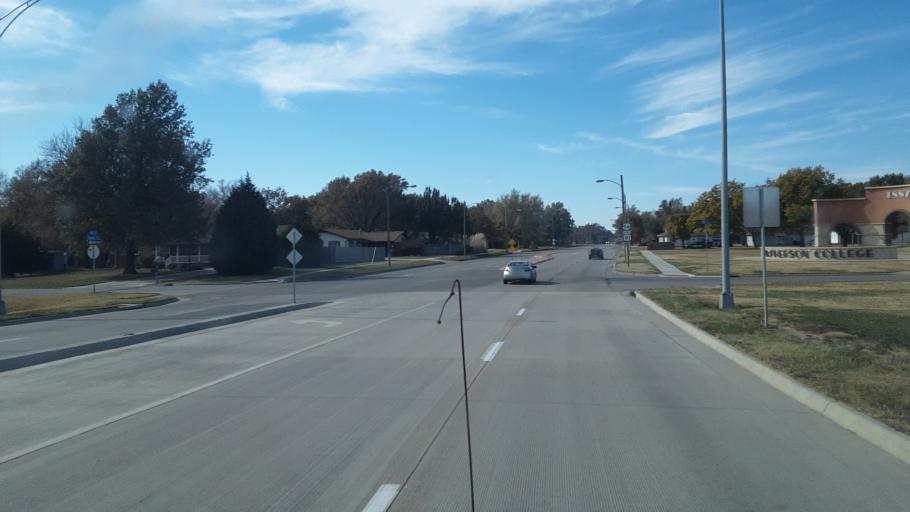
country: US
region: Kansas
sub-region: McPherson County
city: McPherson
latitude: 38.3696
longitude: -97.6415
